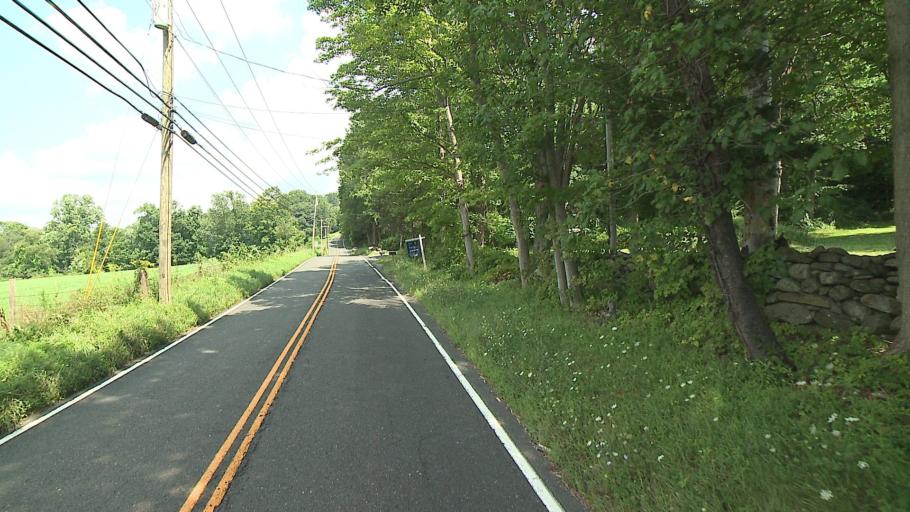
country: US
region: Connecticut
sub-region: Litchfield County
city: New Milford
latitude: 41.6154
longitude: -73.3854
